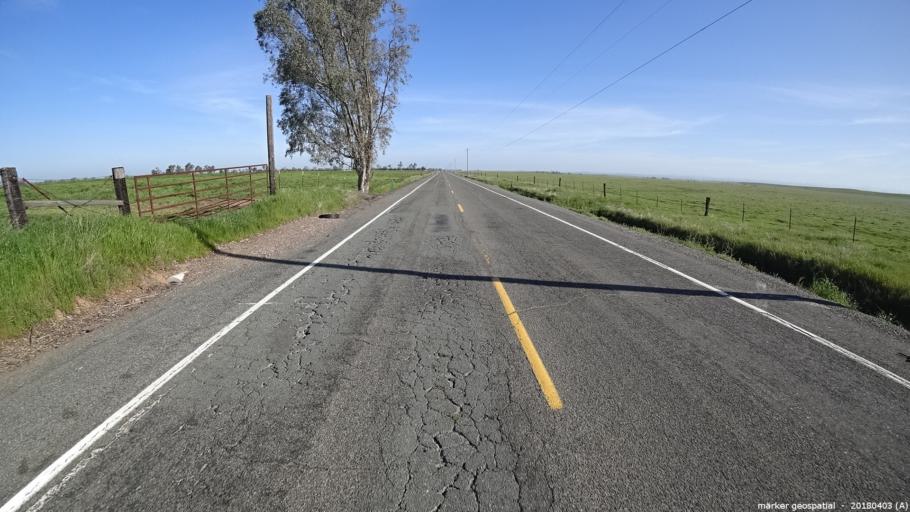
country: US
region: California
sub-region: Sacramento County
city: Clay
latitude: 38.3688
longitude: -121.1685
